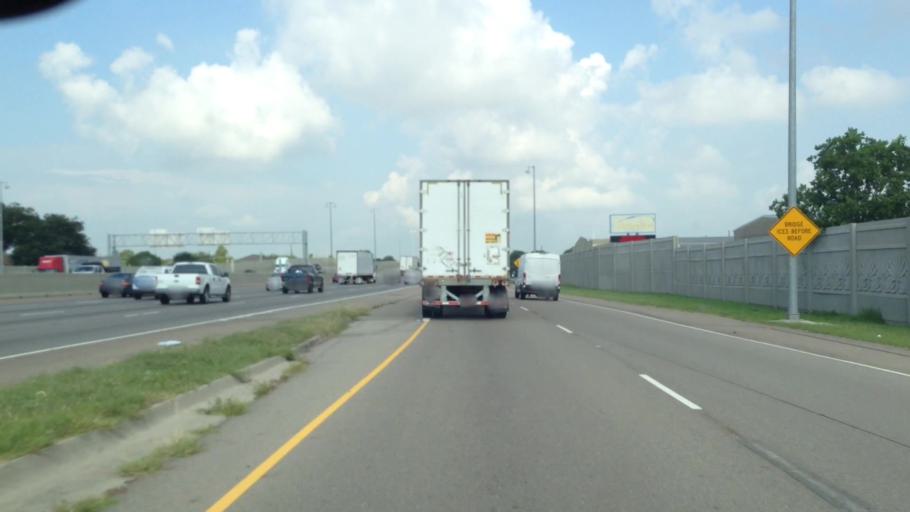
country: US
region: Louisiana
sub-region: Jefferson Parish
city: Metairie Terrace
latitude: 29.9997
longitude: -90.1889
